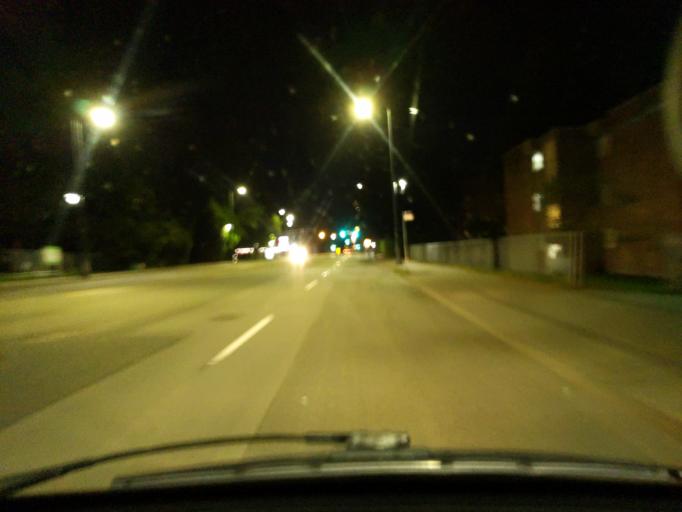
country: CA
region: British Columbia
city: New Westminster
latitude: 49.1917
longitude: -122.8541
